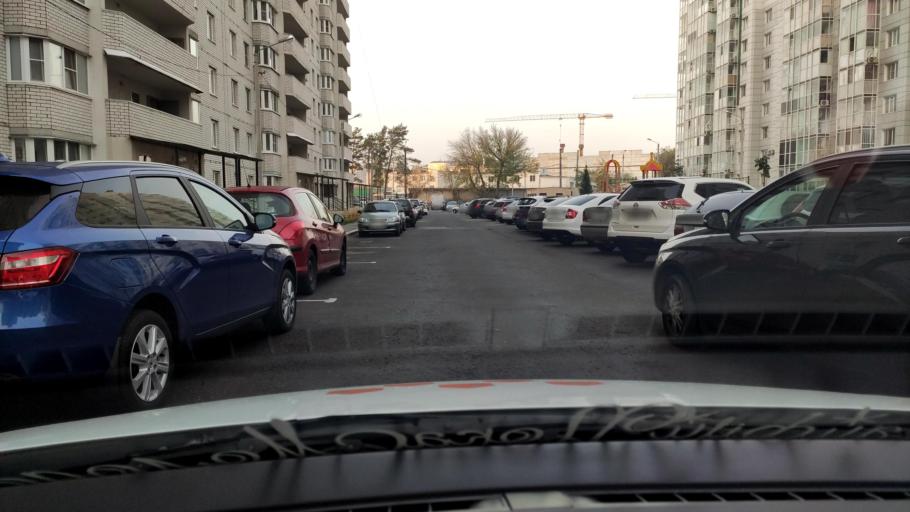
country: RU
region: Voronezj
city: Podgornoye
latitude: 51.6946
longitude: 39.1409
